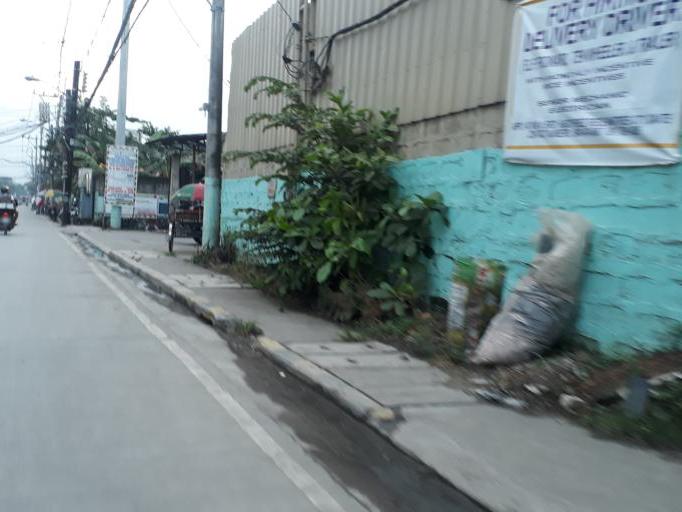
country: PH
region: Central Luzon
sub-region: Province of Bulacan
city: Obando
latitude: 14.7033
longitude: 120.9491
